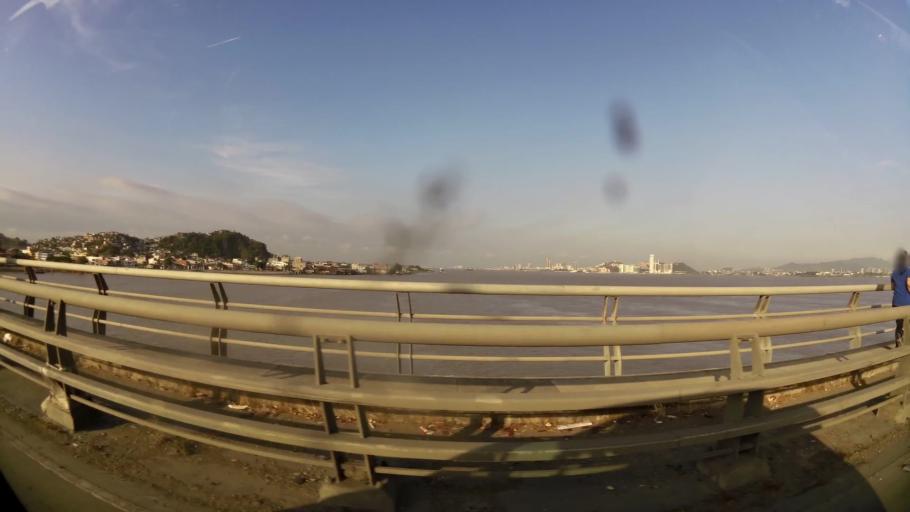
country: EC
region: Guayas
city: Eloy Alfaro
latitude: -2.1620
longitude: -79.8502
